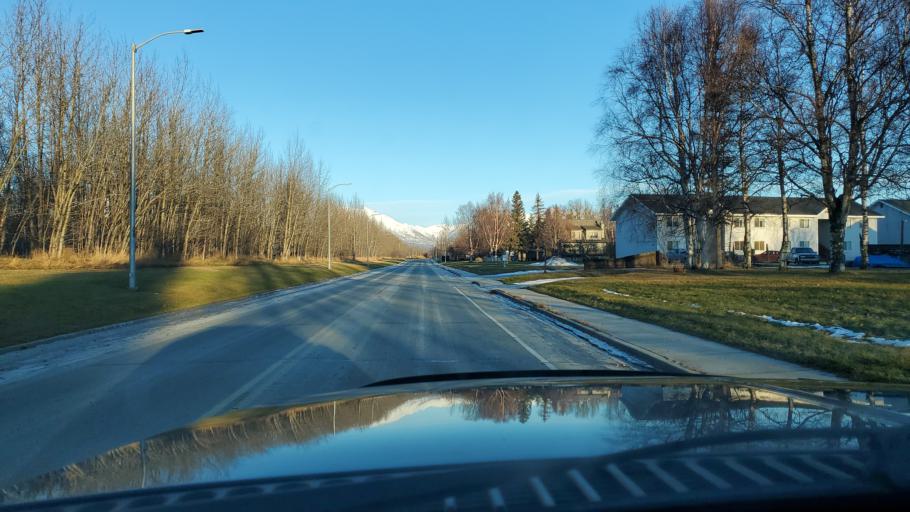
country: US
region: Alaska
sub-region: Matanuska-Susitna Borough
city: Palmer
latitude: 61.6083
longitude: -149.1093
